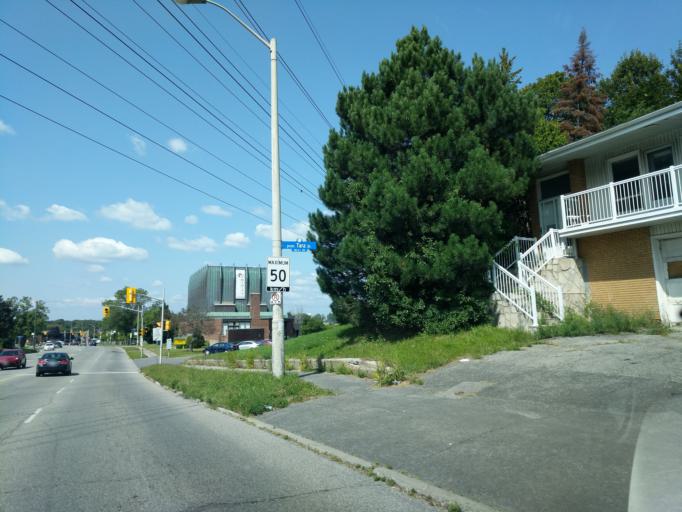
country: CA
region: Ontario
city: Ottawa
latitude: 45.3659
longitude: -75.7505
